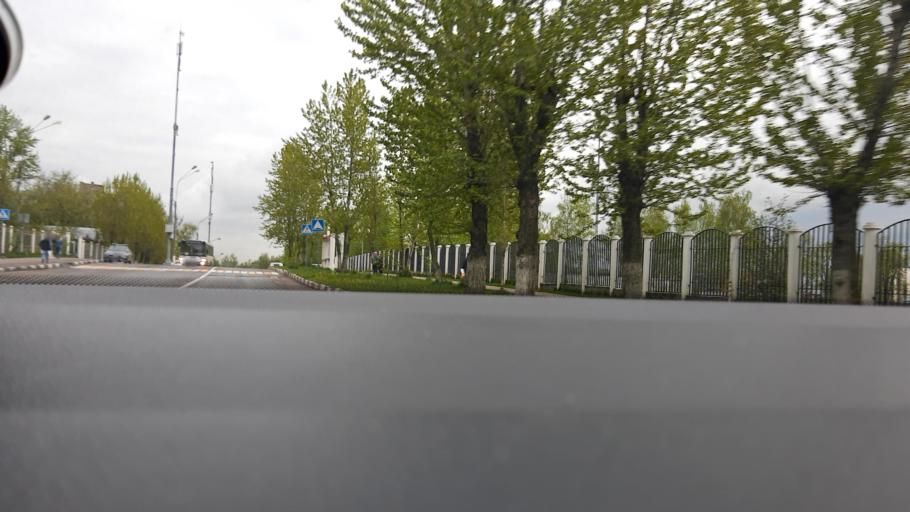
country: RU
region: Moskovskaya
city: Kotel'niki
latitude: 55.6294
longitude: 37.8486
